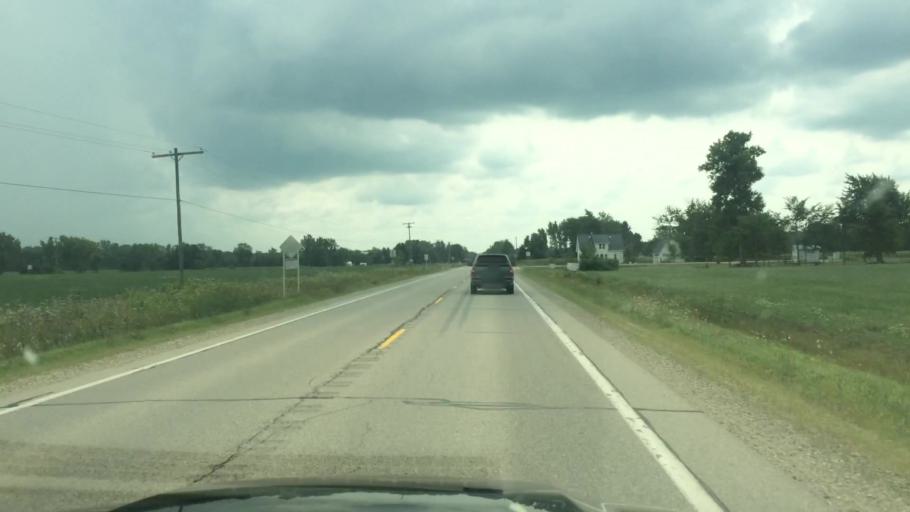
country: US
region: Michigan
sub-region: Tuscola County
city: Cass City
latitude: 43.5178
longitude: -83.0927
